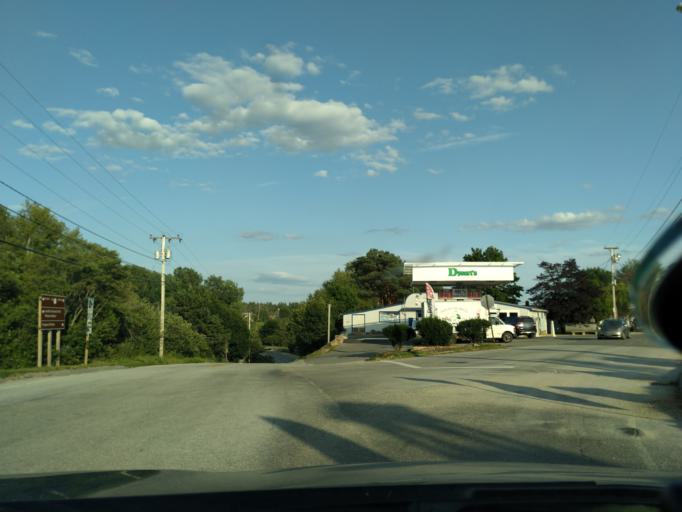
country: US
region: Maine
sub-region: Hancock County
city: Gouldsboro
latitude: 44.3894
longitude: -68.0401
